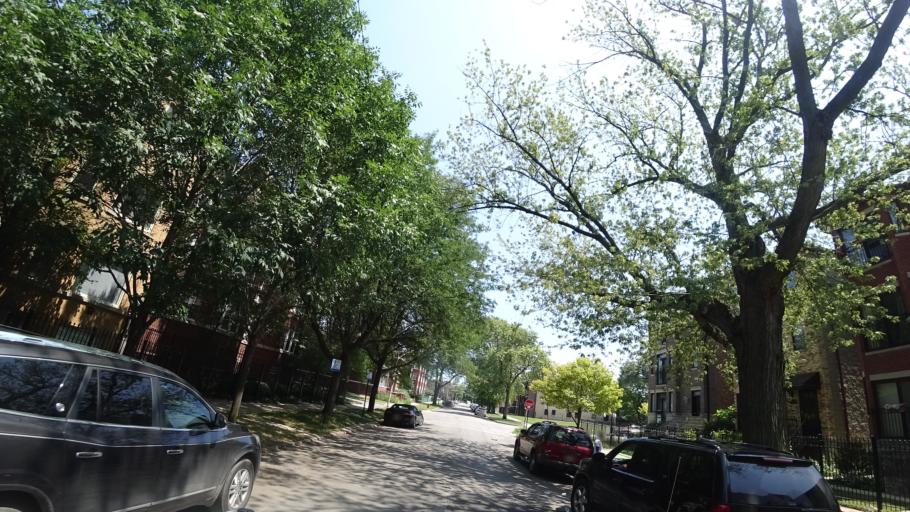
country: US
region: Illinois
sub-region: Cook County
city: Chicago
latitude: 41.7697
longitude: -87.5886
